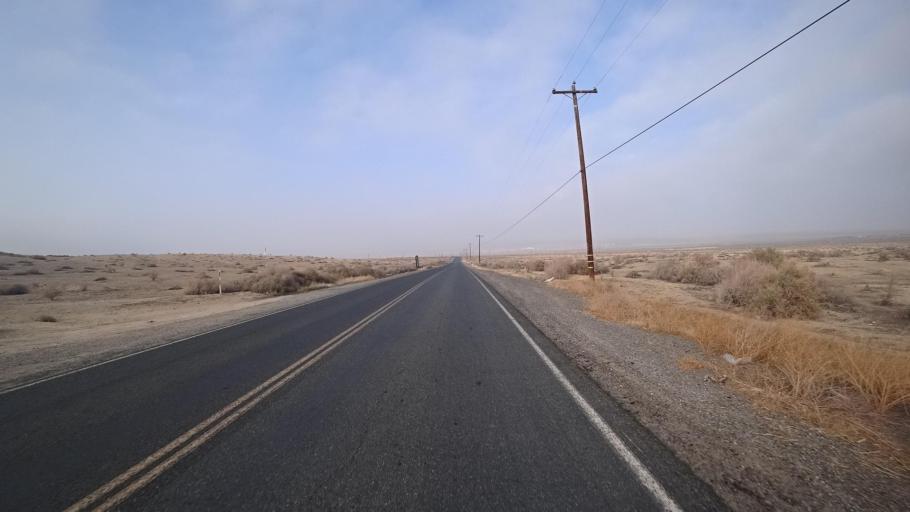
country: US
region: California
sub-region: Kern County
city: Ford City
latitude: 35.2038
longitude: -119.4456
